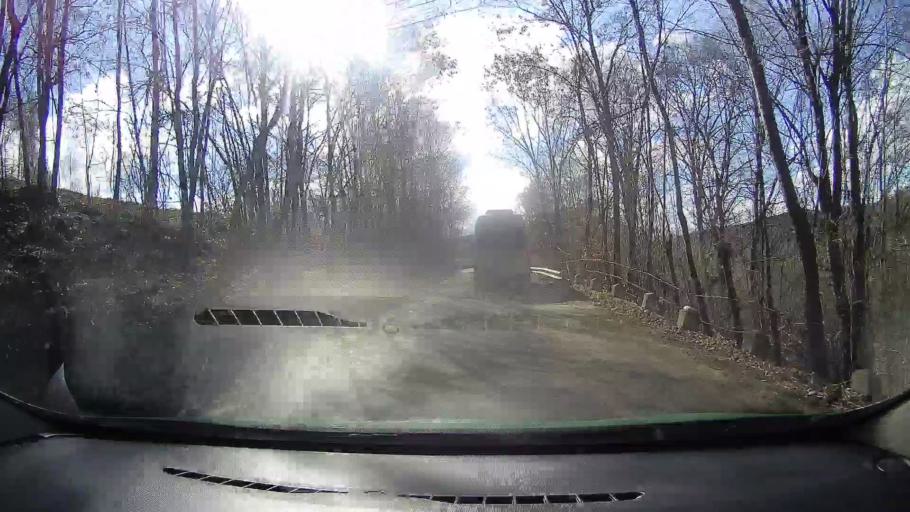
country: RO
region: Dambovita
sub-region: Comuna Runcu
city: Badeni
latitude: 45.1476
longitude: 25.4037
